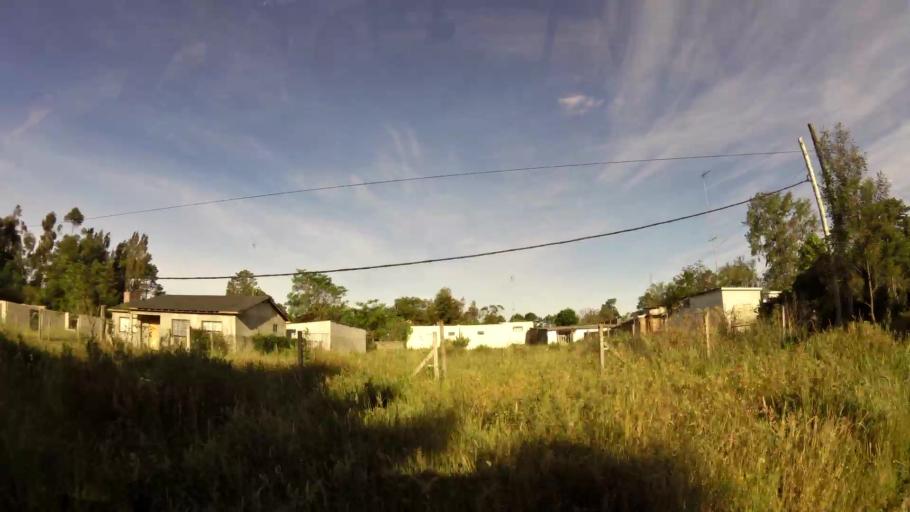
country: UY
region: Canelones
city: Empalme Olmos
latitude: -34.7745
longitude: -55.8564
